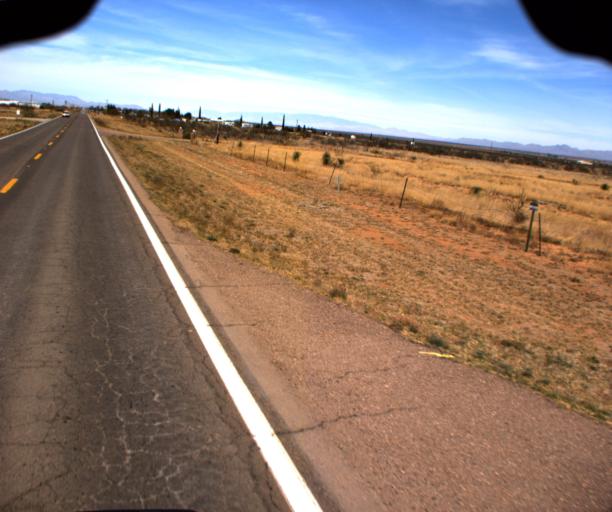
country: US
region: Arizona
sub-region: Cochise County
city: Willcox
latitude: 31.9508
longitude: -109.8362
